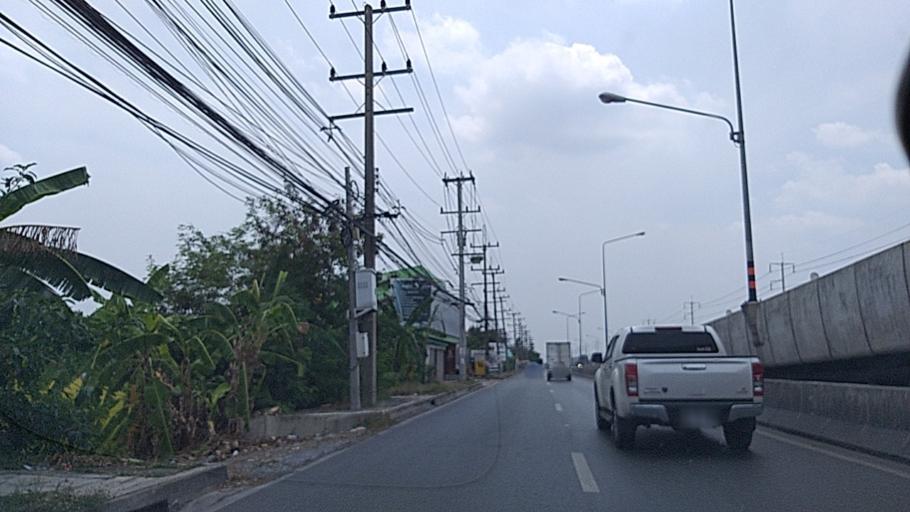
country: TH
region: Nakhon Pathom
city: Salaya
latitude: 13.7847
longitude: 100.3029
